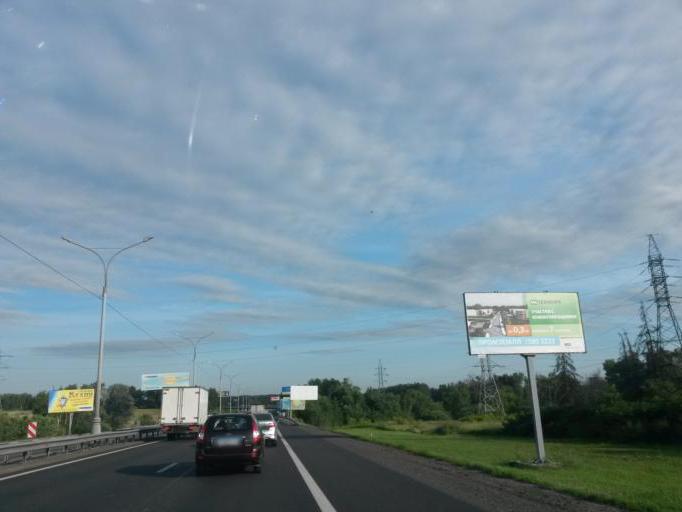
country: RU
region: Moskovskaya
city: Petrovskaya
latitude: 55.5647
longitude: 37.7707
